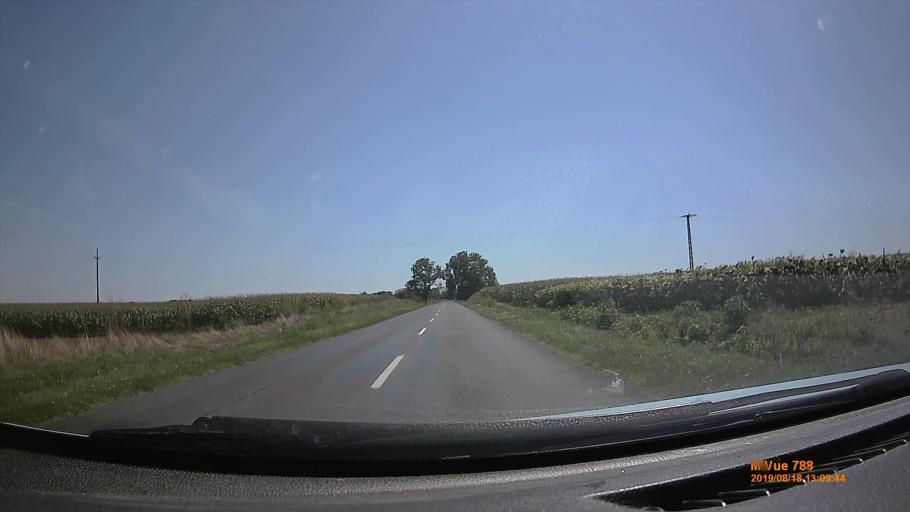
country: HU
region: Fejer
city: Kaloz
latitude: 46.9235
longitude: 18.5124
